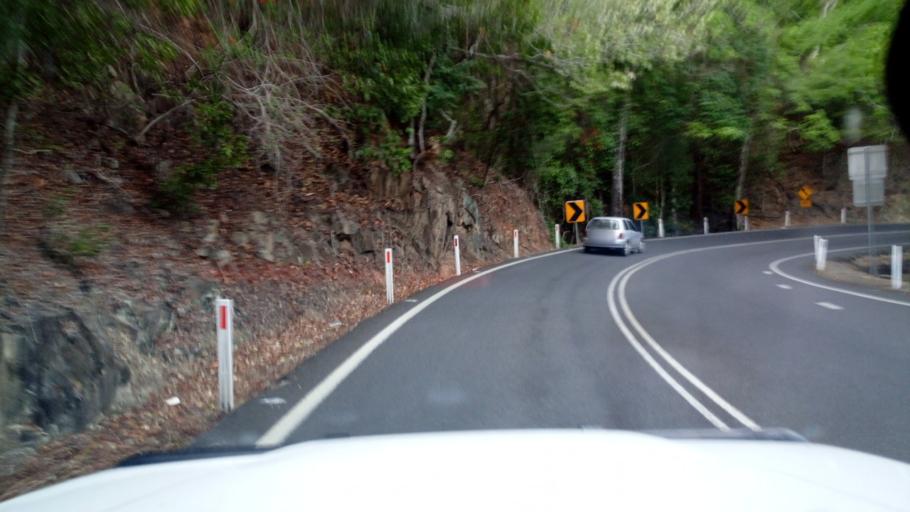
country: AU
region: Queensland
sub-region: Cairns
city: Redlynch
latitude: -16.8467
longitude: 145.6830
